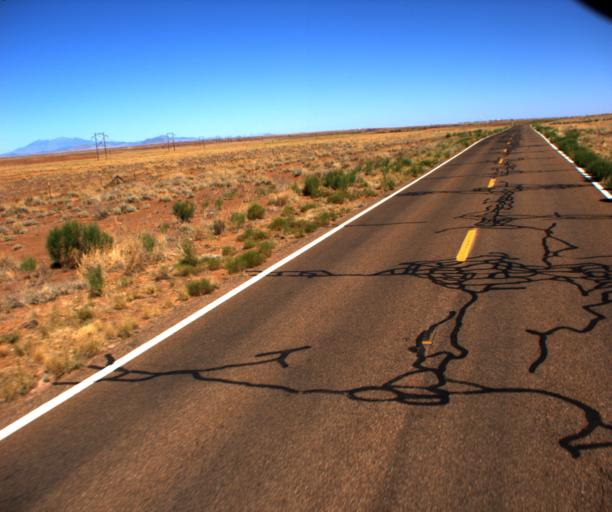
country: US
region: Arizona
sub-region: Coconino County
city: LeChee
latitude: 35.2575
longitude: -110.9643
